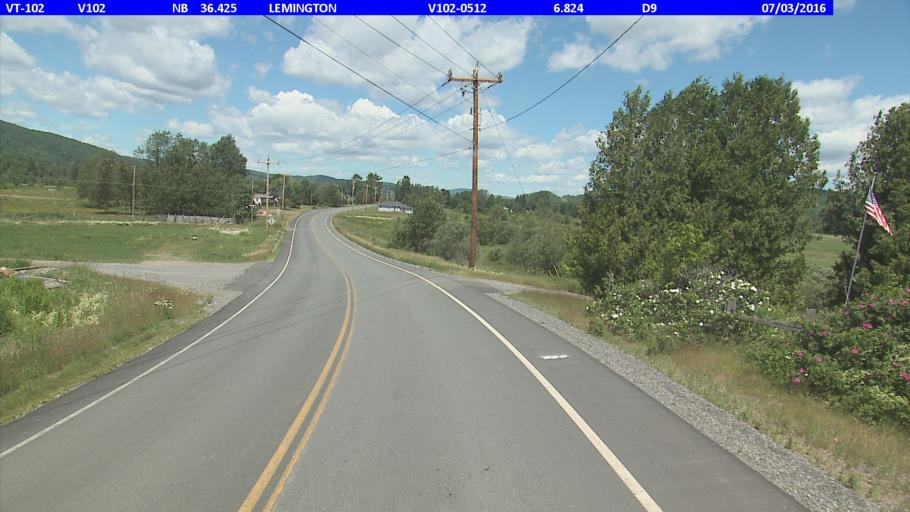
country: US
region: New Hampshire
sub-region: Coos County
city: Colebrook
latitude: 44.9046
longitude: -71.5018
